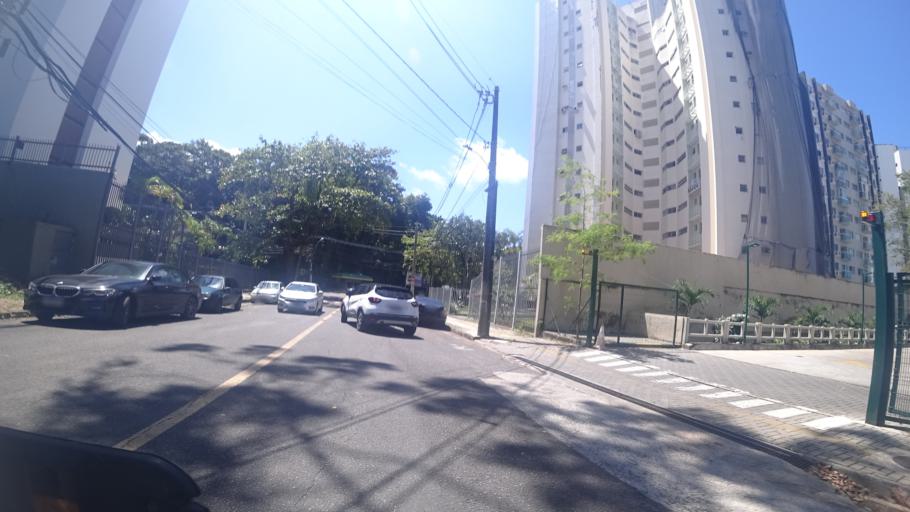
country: BR
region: Bahia
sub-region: Salvador
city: Salvador
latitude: -12.9933
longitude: -38.4656
